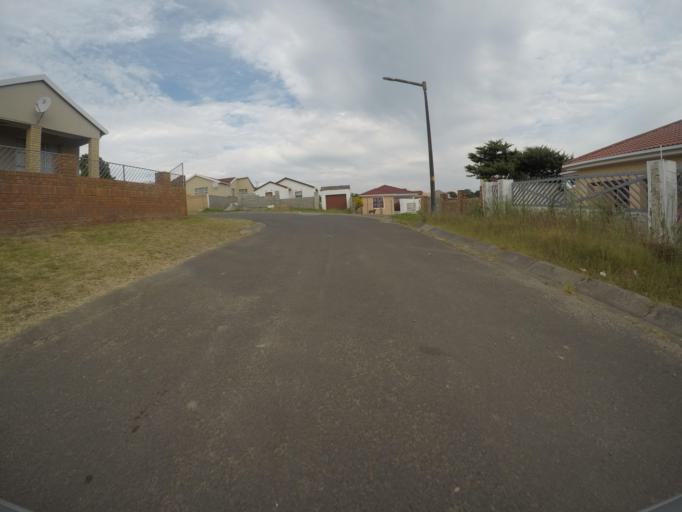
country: ZA
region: Eastern Cape
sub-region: Buffalo City Metropolitan Municipality
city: East London
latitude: -32.9760
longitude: 27.8584
